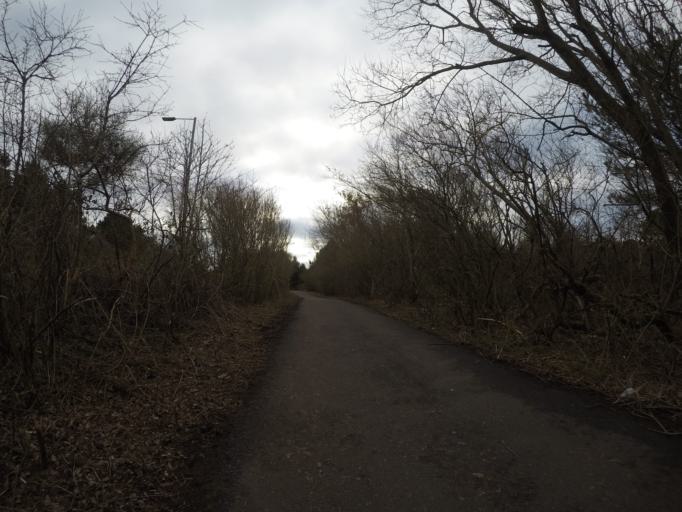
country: GB
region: Scotland
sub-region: North Ayrshire
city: Irvine
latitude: 55.5976
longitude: -4.6761
